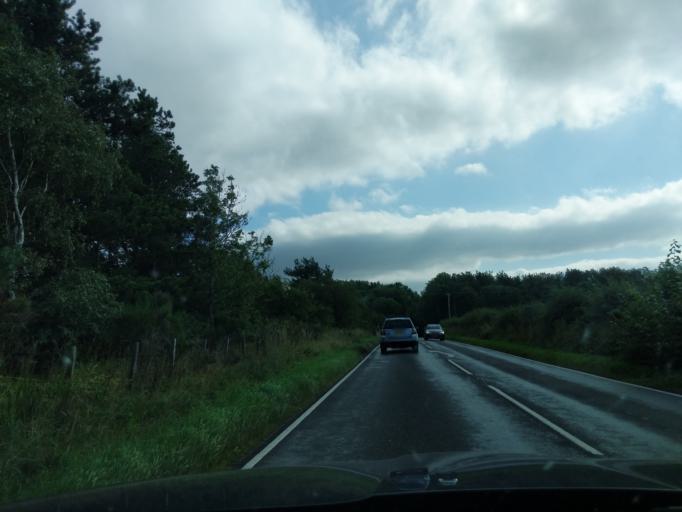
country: GB
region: England
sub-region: Northumberland
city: Ford
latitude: 55.5846
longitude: -2.0919
